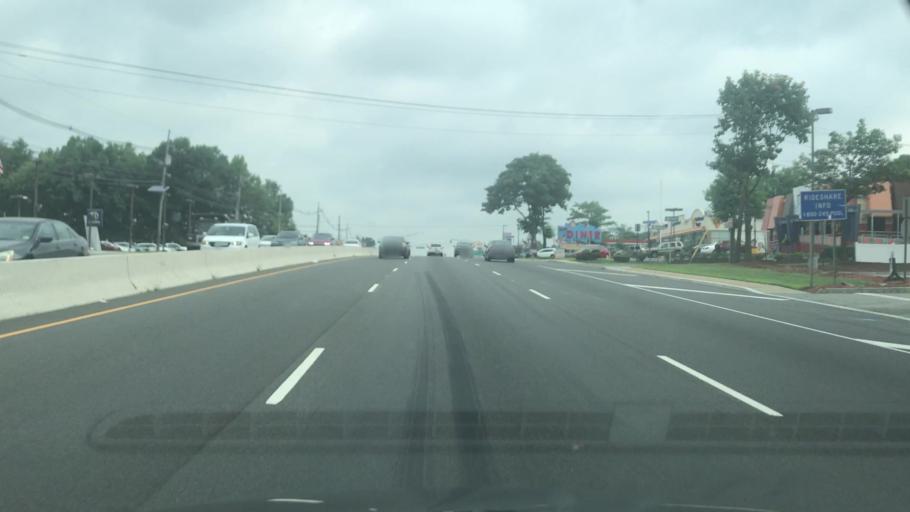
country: US
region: New Jersey
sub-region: Passaic County
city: Wayne
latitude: 40.9312
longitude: -74.2688
